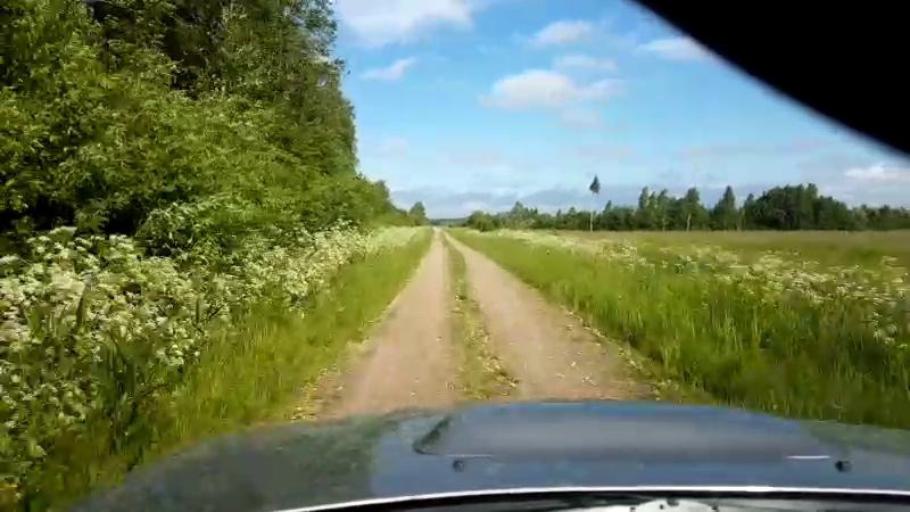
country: EE
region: Paernumaa
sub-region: Sindi linn
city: Sindi
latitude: 58.4869
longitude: 24.6613
